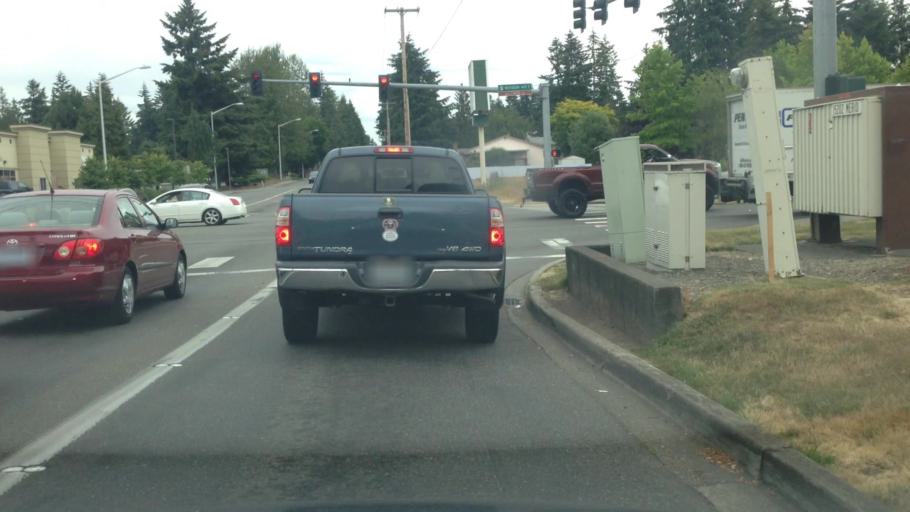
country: US
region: Washington
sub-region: Pierce County
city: South Hill
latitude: 47.1183
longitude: -122.2938
